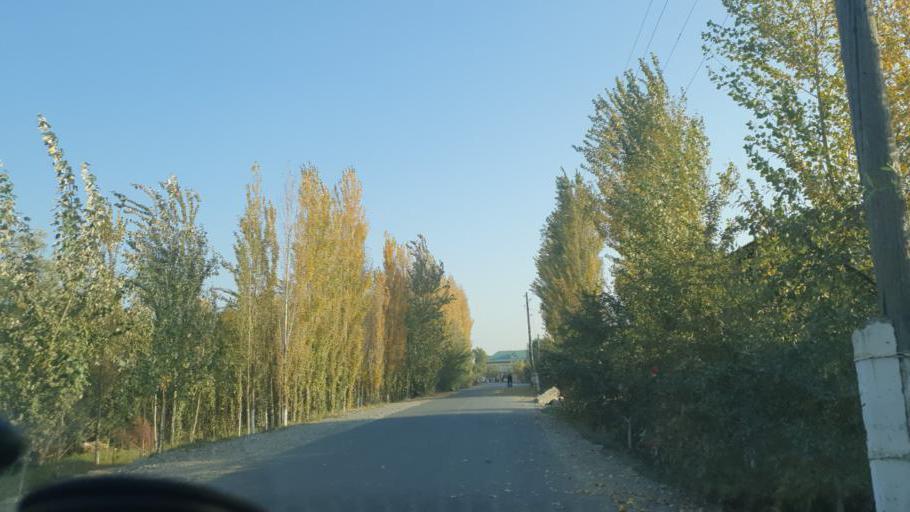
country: UZ
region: Fergana
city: Beshariq
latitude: 40.4638
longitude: 70.5431
